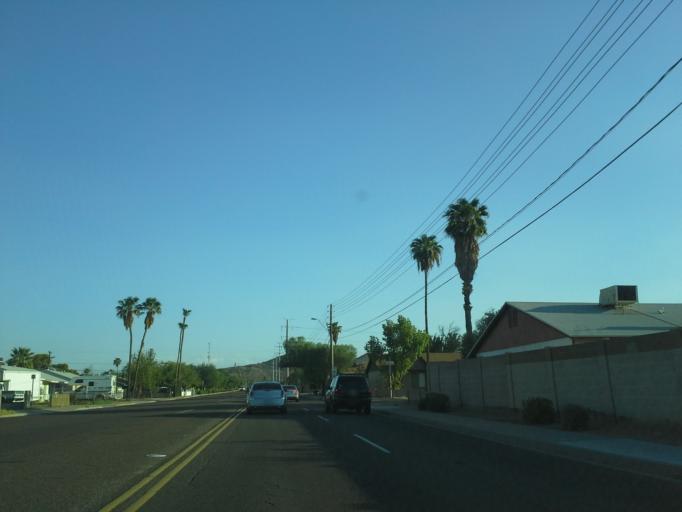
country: US
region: Arizona
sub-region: Maricopa County
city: Guadalupe
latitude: 33.3851
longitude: -111.9784
